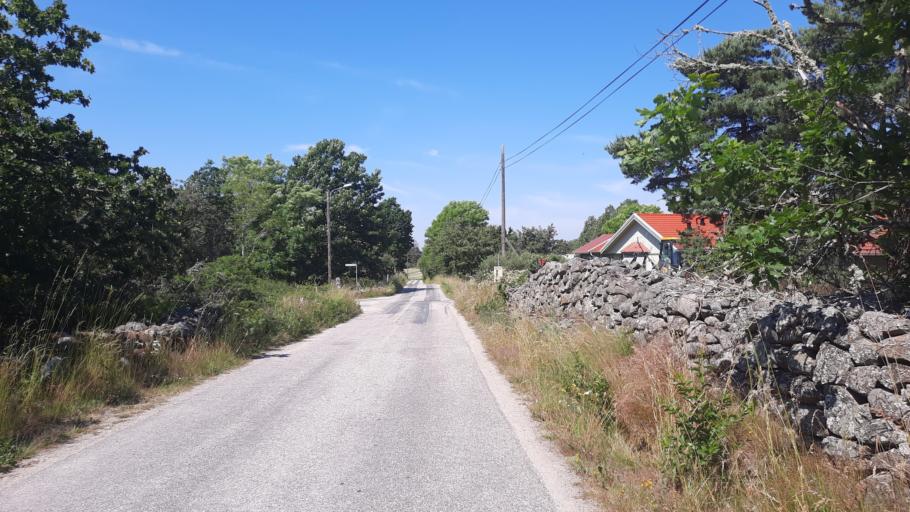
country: SE
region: Blekinge
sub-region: Karlskrona Kommun
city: Jaemjoe
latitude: 56.1503
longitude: 15.7670
